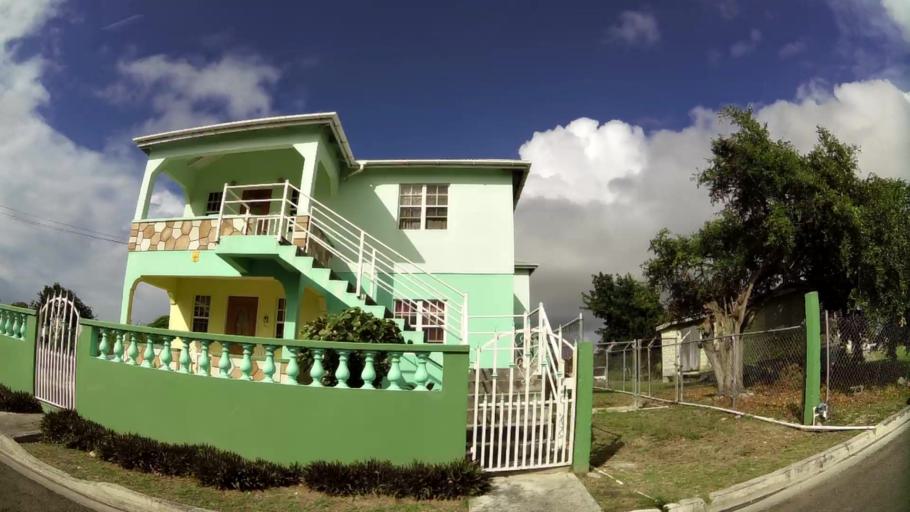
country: AG
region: Saint John
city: Saint John's
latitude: 17.1200
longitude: -61.8287
